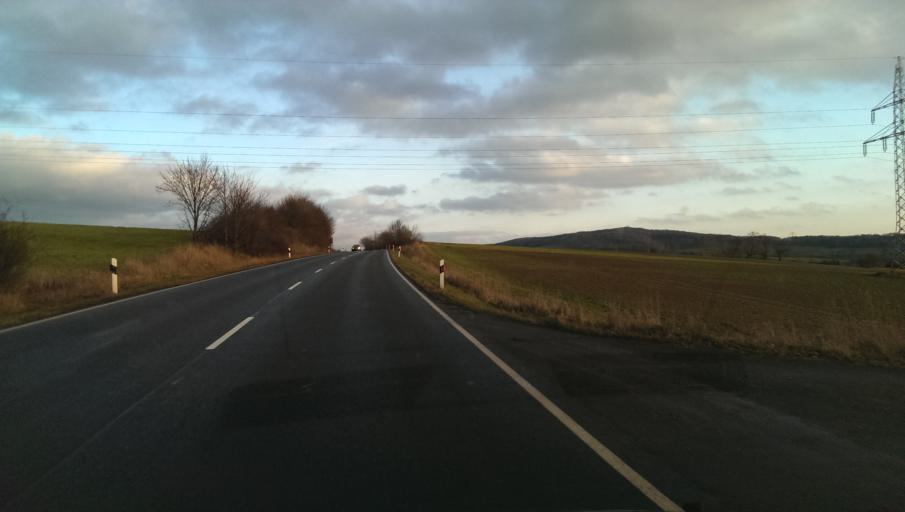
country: DE
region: Lower Saxony
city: Eimen
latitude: 51.8690
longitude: 9.8316
